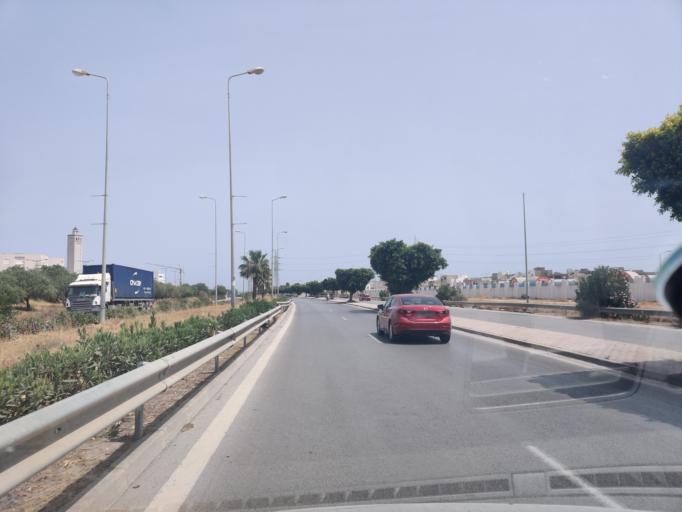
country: TN
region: Tunis
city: La Goulette
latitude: 36.8443
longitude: 10.3005
